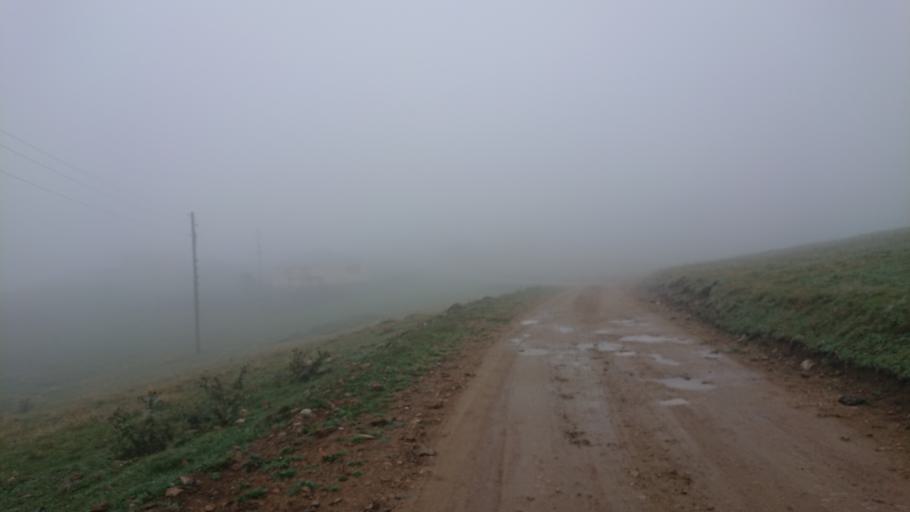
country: TR
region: Gumushane
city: Kurtun
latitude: 40.6728
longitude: 38.9944
